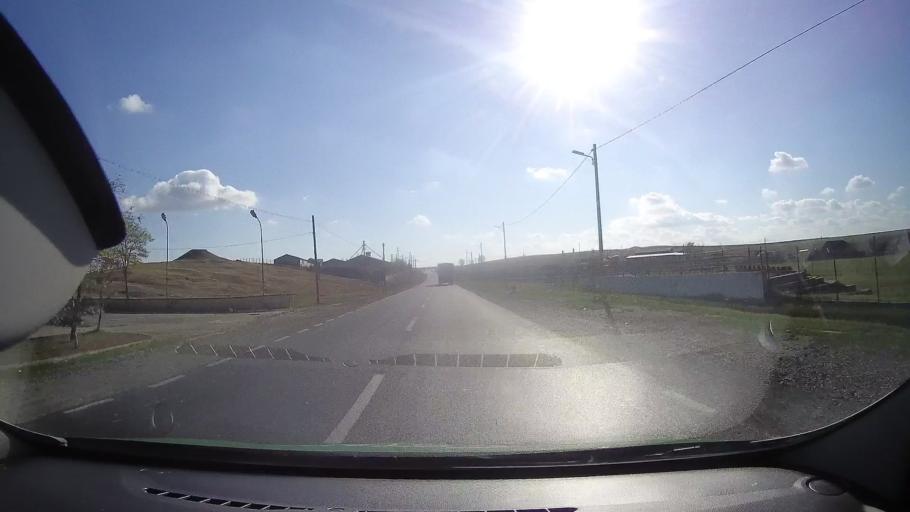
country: RO
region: Tulcea
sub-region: Comuna Baia
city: Baia
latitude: 44.7194
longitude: 28.6800
